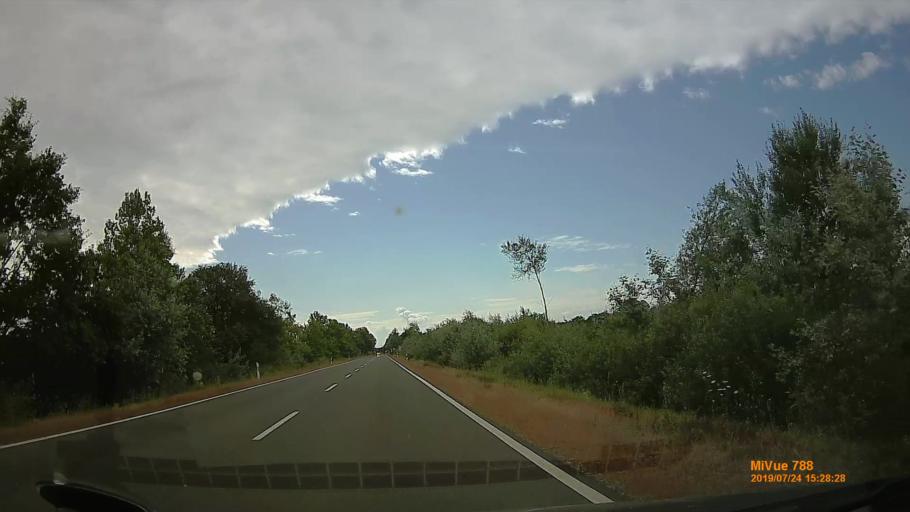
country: HU
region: Szabolcs-Szatmar-Bereg
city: Tarpa
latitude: 48.1610
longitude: 22.4766
